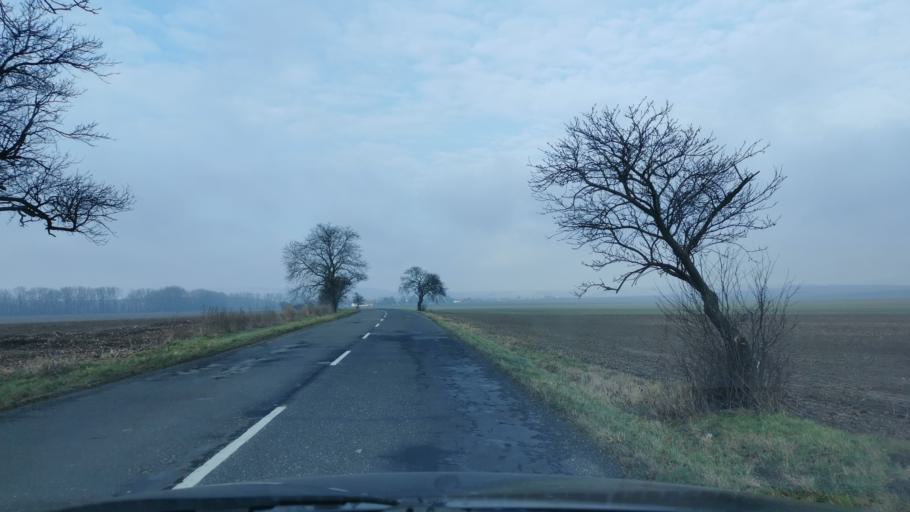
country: SK
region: Trnavsky
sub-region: Okres Senica
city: Senica
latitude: 48.6939
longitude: 17.3546
